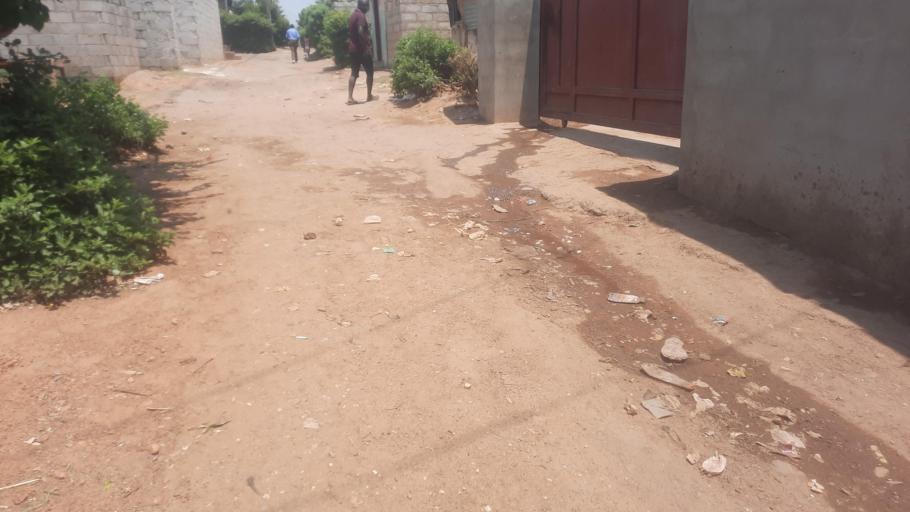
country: ZM
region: Lusaka
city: Lusaka
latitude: -15.4026
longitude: 28.3711
